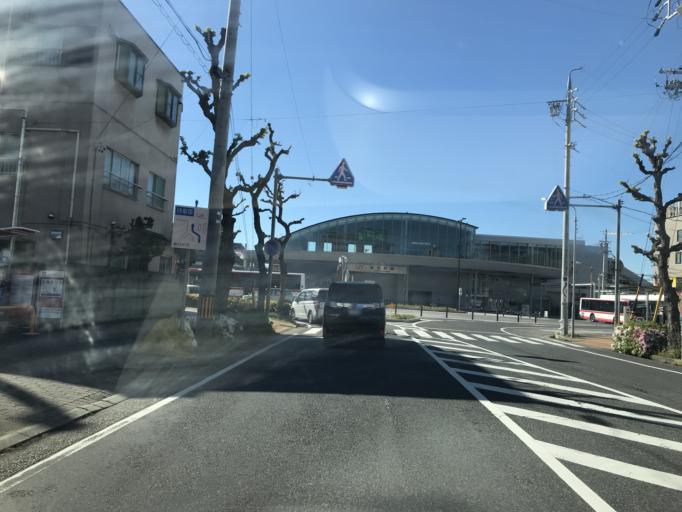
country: JP
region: Aichi
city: Kasugai
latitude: 35.2441
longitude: 136.9847
